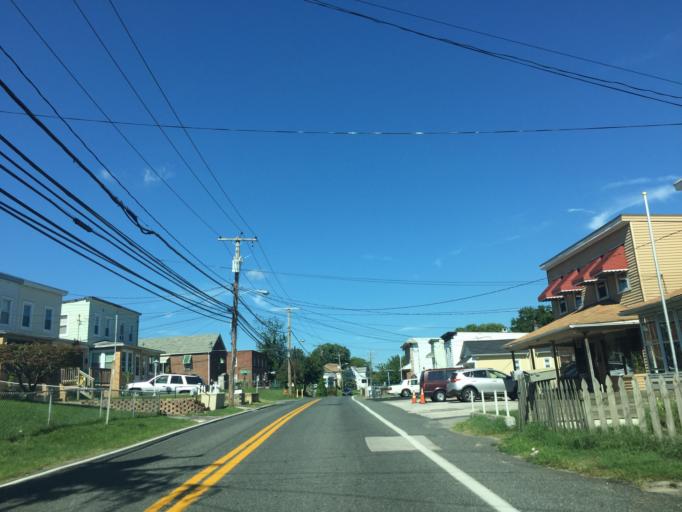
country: US
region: Maryland
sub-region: Baltimore County
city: Rosedale
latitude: 39.2913
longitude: -76.5144
